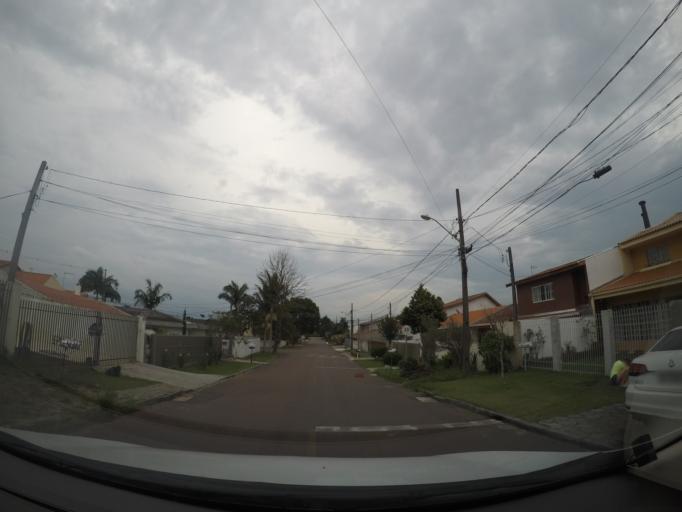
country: BR
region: Parana
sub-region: Curitiba
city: Curitiba
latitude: -25.4710
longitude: -49.2430
